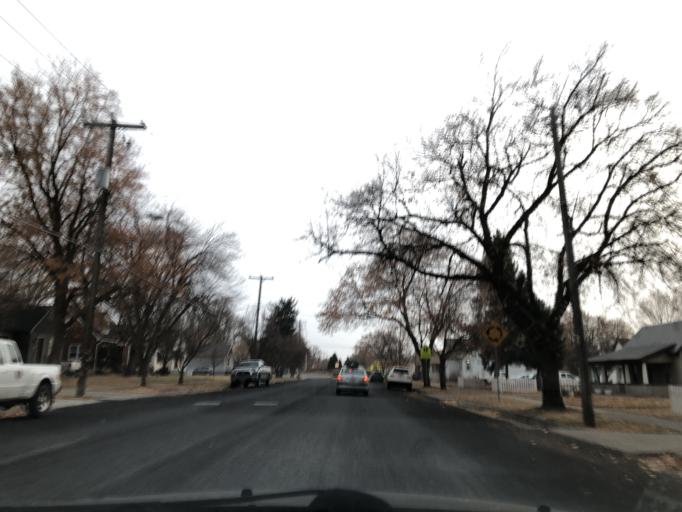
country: US
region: Utah
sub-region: Cache County
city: Logan
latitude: 41.7423
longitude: -111.8296
